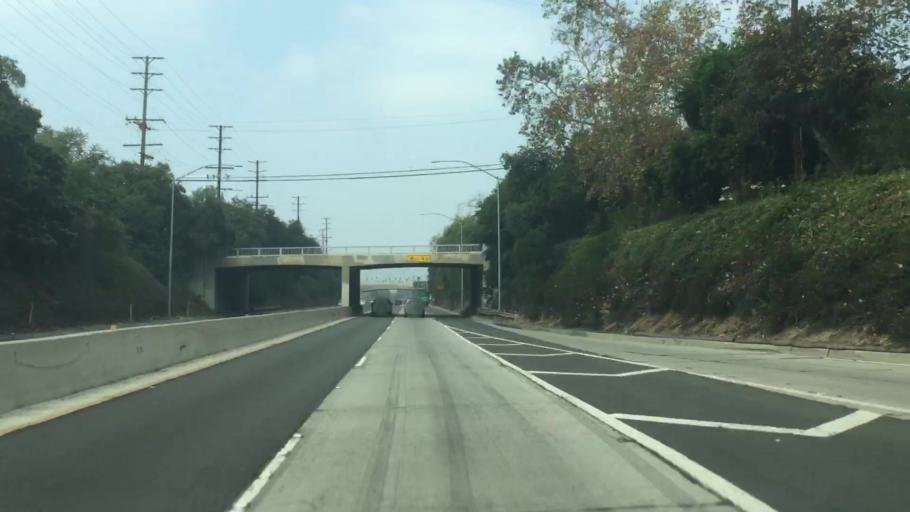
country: US
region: California
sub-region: Los Angeles County
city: South Pasadena
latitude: 34.1192
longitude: -118.1624
